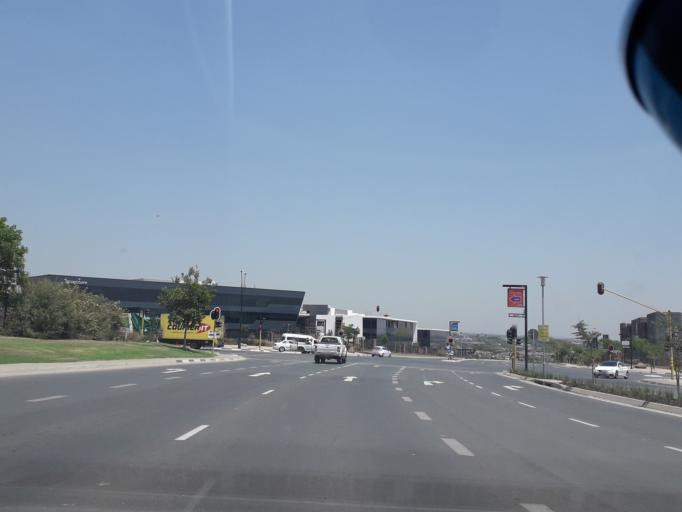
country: ZA
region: Gauteng
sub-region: City of Johannesburg Metropolitan Municipality
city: Midrand
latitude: -26.0133
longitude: 28.1001
